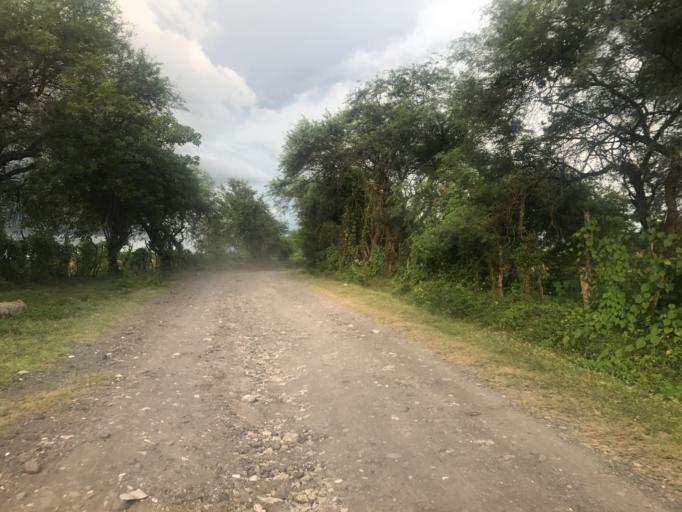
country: MX
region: Morelos
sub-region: Axochiapan
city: Quebrantadero
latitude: 18.5172
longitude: -98.8009
